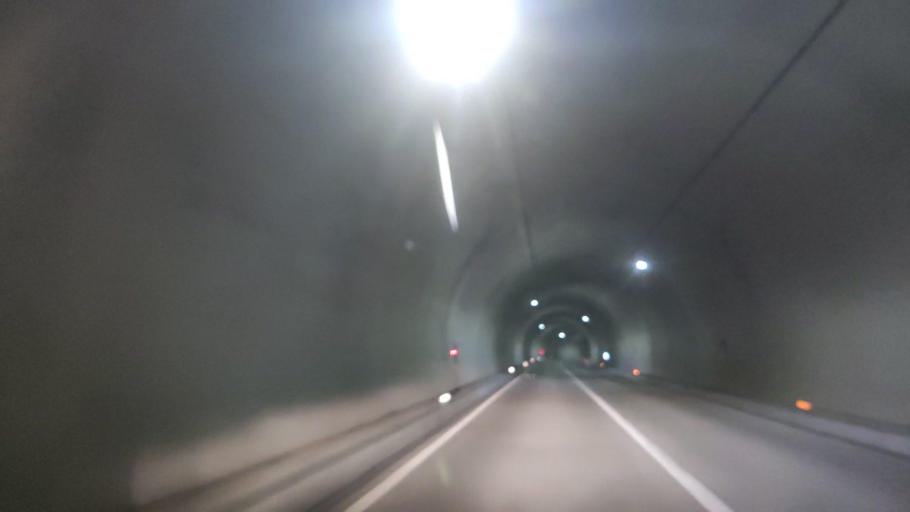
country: JP
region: Tottori
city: Tottori
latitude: 35.3523
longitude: 134.4732
